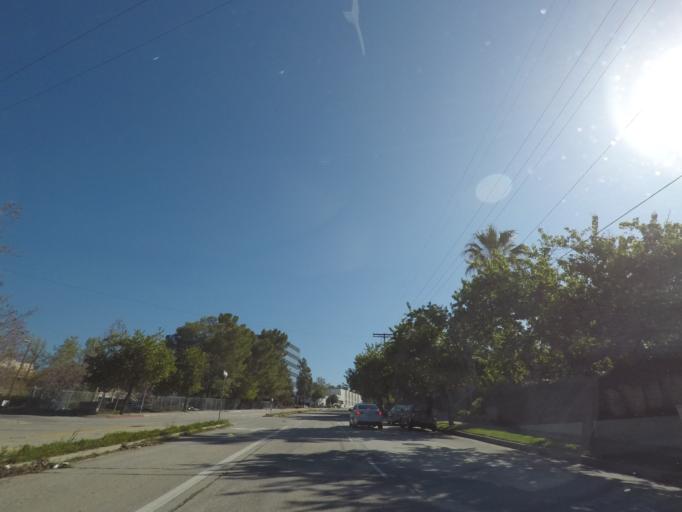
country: US
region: California
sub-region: Los Angeles County
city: Pasadena
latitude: 34.1396
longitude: -118.1850
